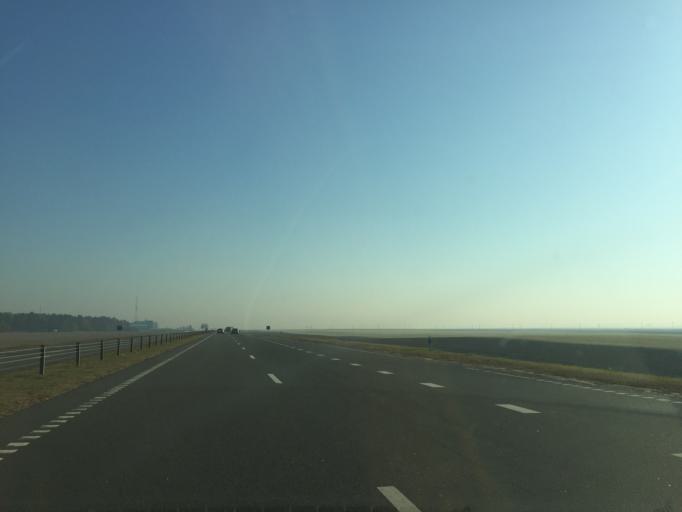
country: BY
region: Gomel
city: Kastsyukowka
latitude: 52.4922
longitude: 30.8355
